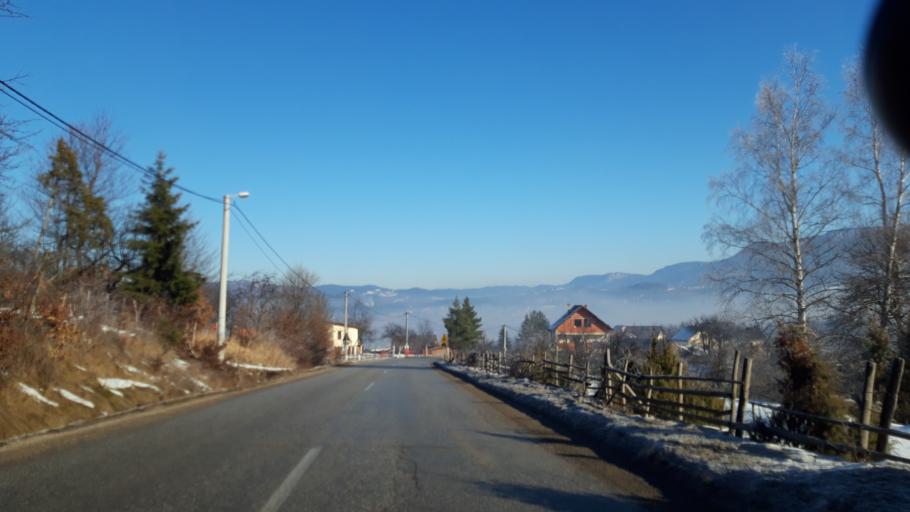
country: BA
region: Republika Srpska
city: Koran
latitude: 43.8067
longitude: 18.5537
